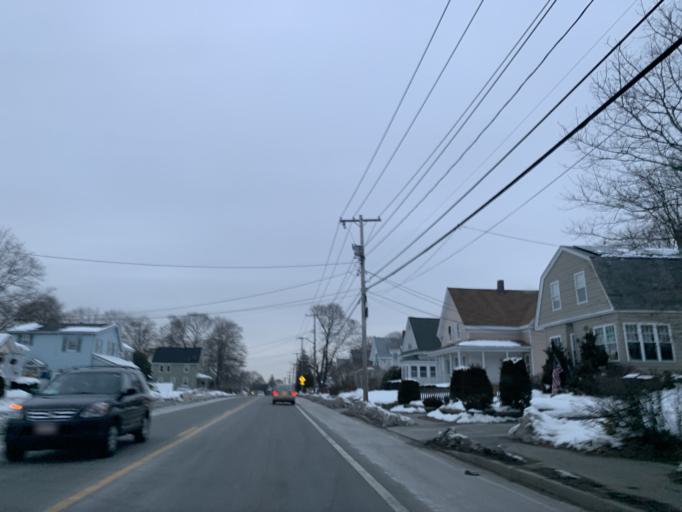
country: US
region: Massachusetts
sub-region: Norfolk County
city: Stoughton
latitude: 42.1211
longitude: -71.0942
